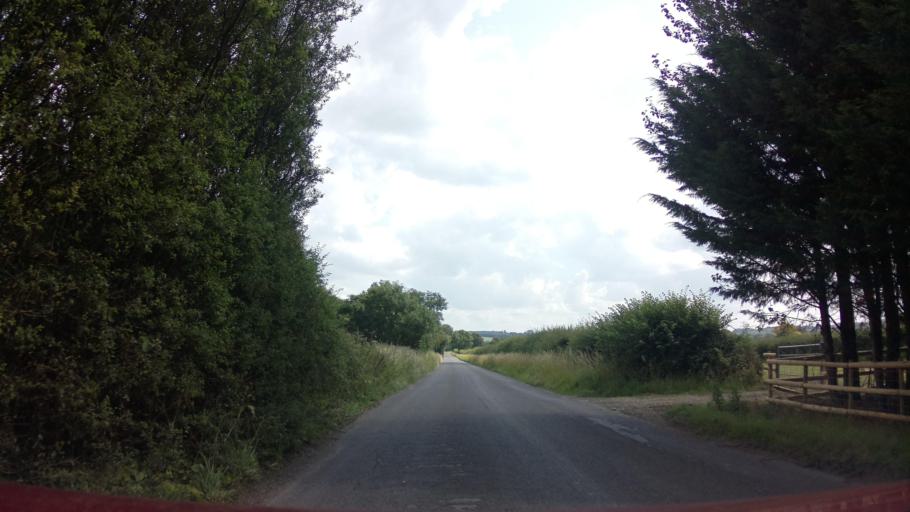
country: GB
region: England
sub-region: Wiltshire
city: Minety
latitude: 51.5886
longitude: -1.9334
